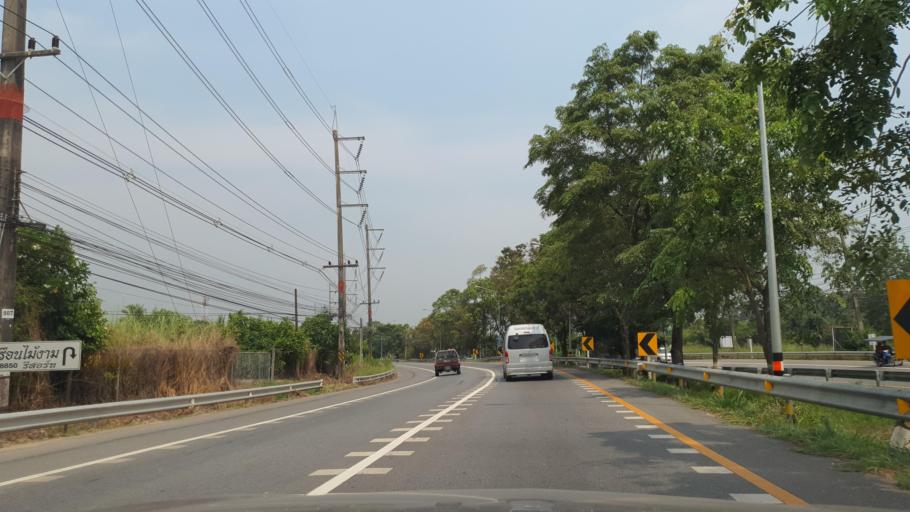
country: TH
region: Rayong
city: Rayong
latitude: 12.6400
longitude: 101.3624
